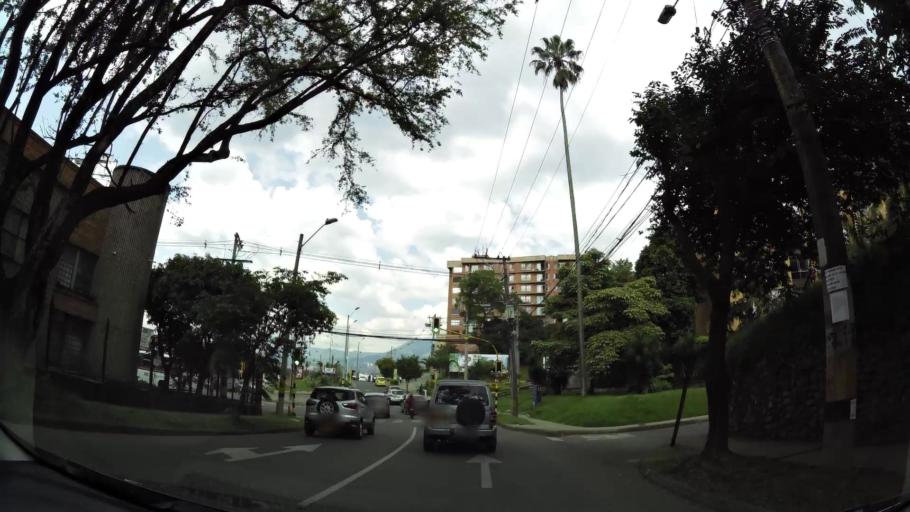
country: CO
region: Antioquia
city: Sabaneta
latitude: 6.1599
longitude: -75.6025
